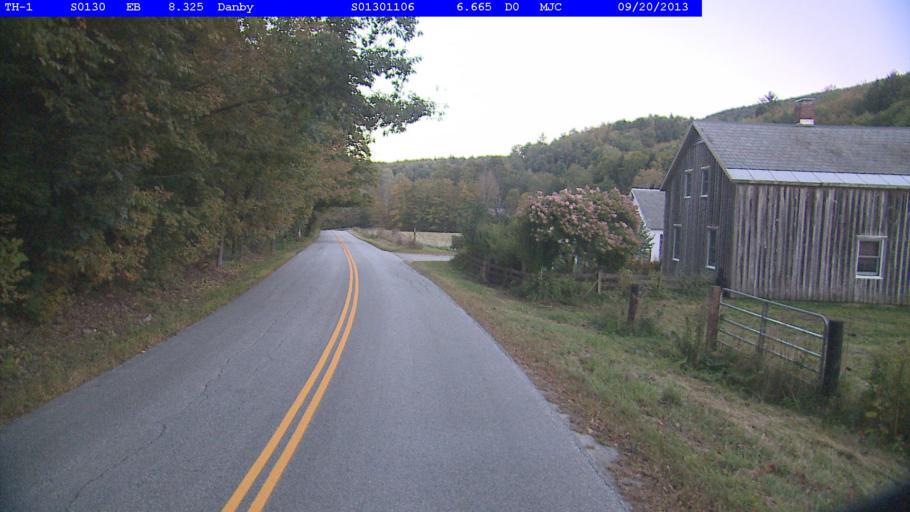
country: US
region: Vermont
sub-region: Bennington County
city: Manchester Center
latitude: 43.3400
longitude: -73.0228
